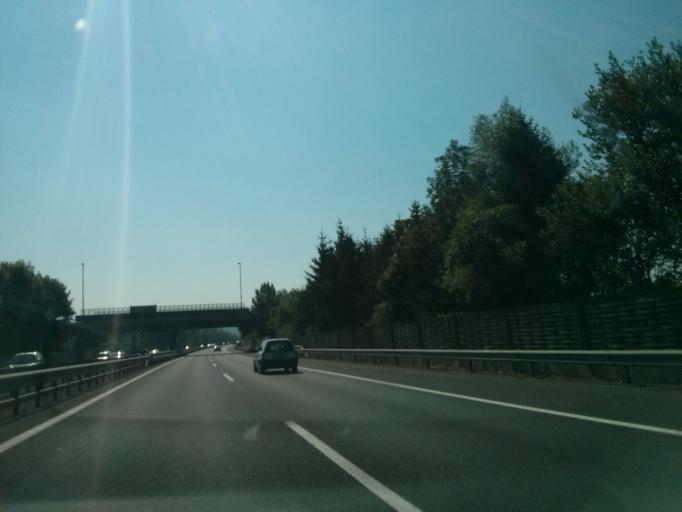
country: SI
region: Ljubljana
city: Ljubljana
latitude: 46.0233
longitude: 14.5093
